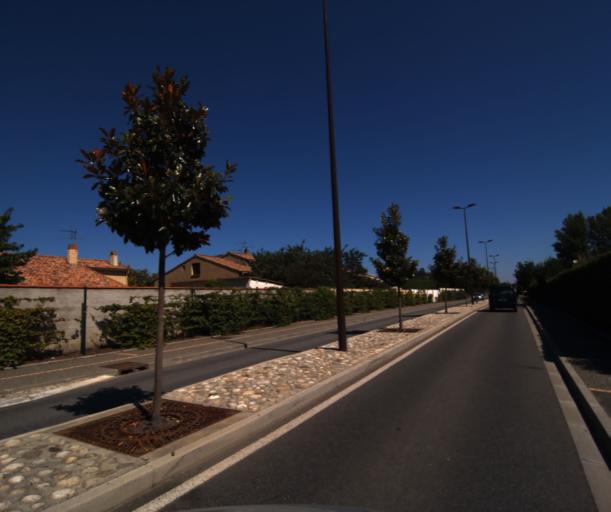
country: FR
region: Midi-Pyrenees
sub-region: Departement de la Haute-Garonne
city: Muret
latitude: 43.4708
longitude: 1.3239
